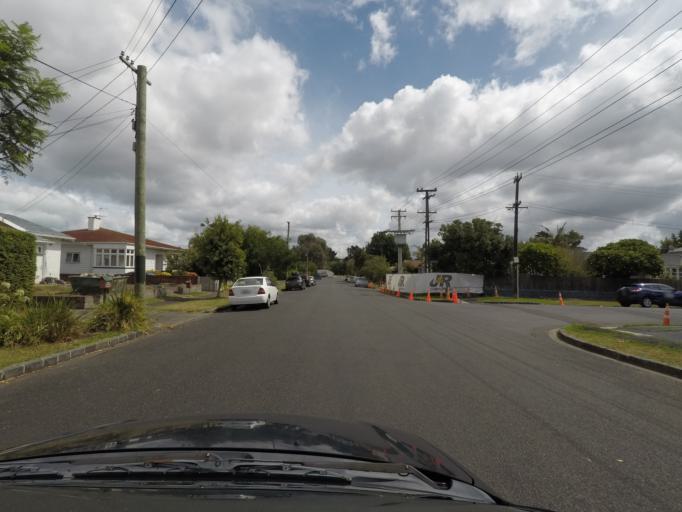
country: NZ
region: Auckland
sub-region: Auckland
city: Rosebank
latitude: -36.8876
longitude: 174.7073
